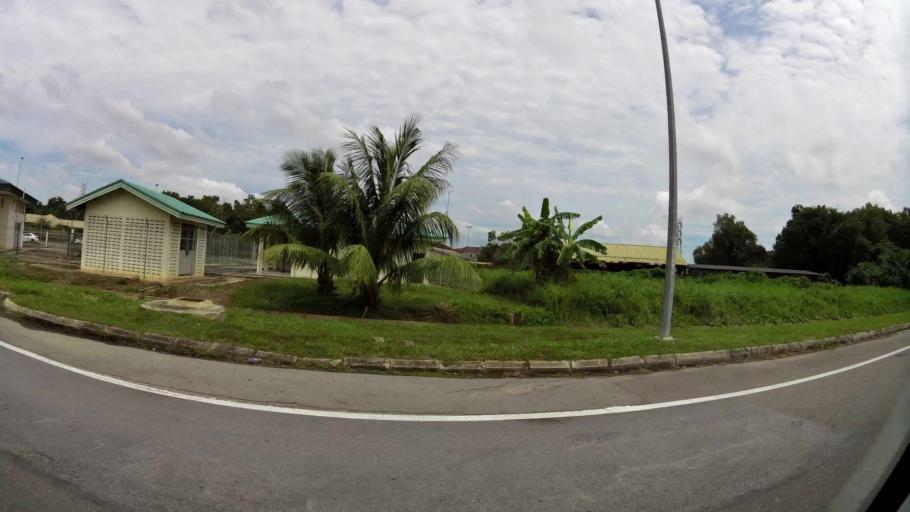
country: BN
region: Brunei and Muara
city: Bandar Seri Begawan
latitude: 4.9499
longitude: 114.9429
